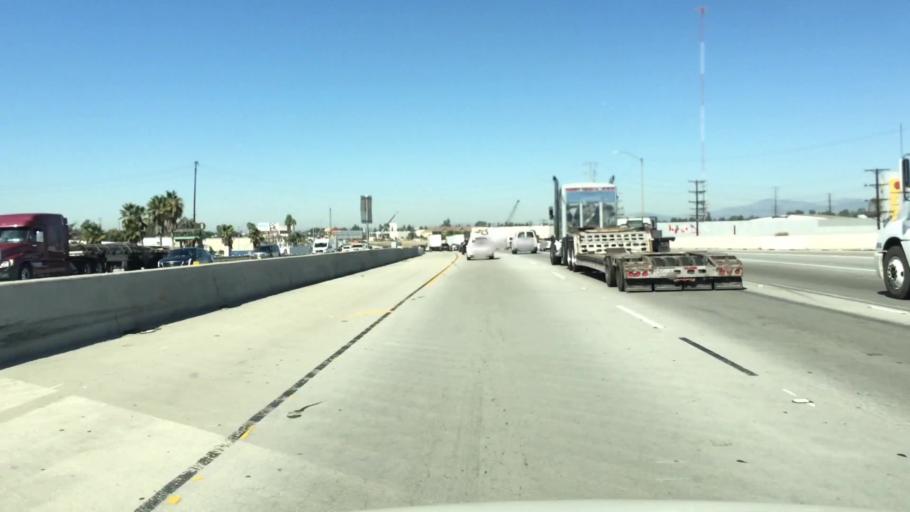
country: US
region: California
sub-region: Orange County
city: Buena Park
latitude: 33.8733
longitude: -118.0096
